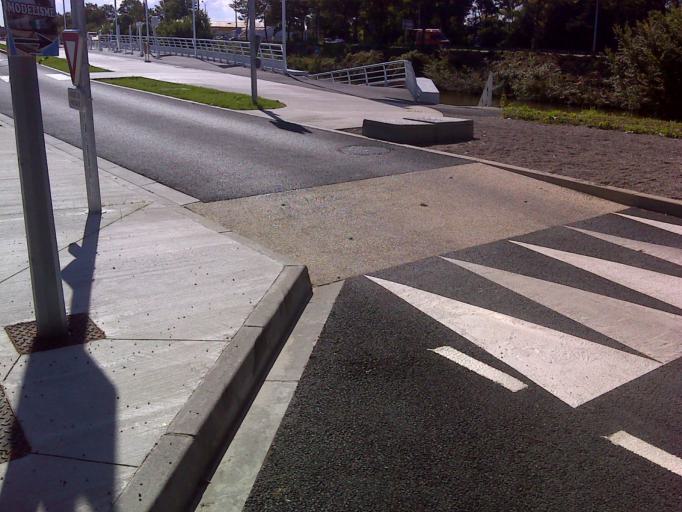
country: FR
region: Nord-Pas-de-Calais
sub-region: Departement du Nord
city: Coudekerque-Branche
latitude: 51.0133
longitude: 2.3797
